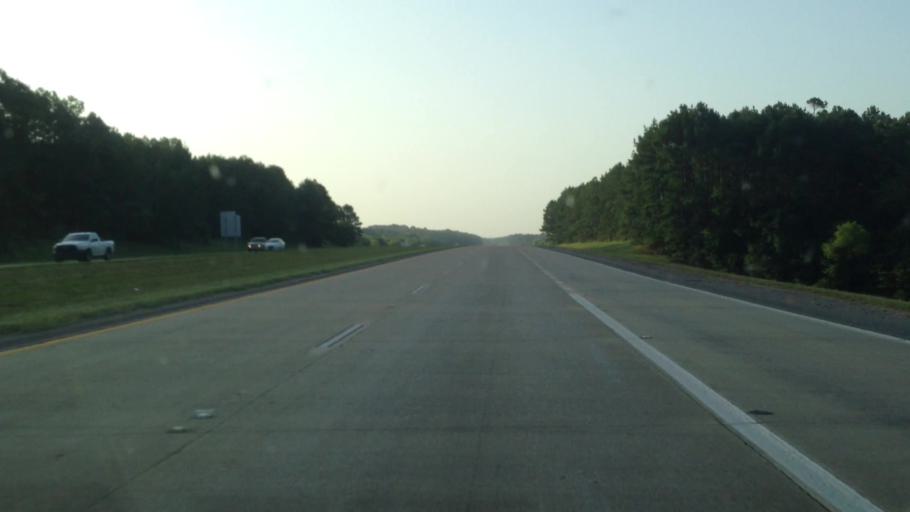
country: US
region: Louisiana
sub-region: Grant Parish
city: Colfax
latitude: 31.4909
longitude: -92.8569
